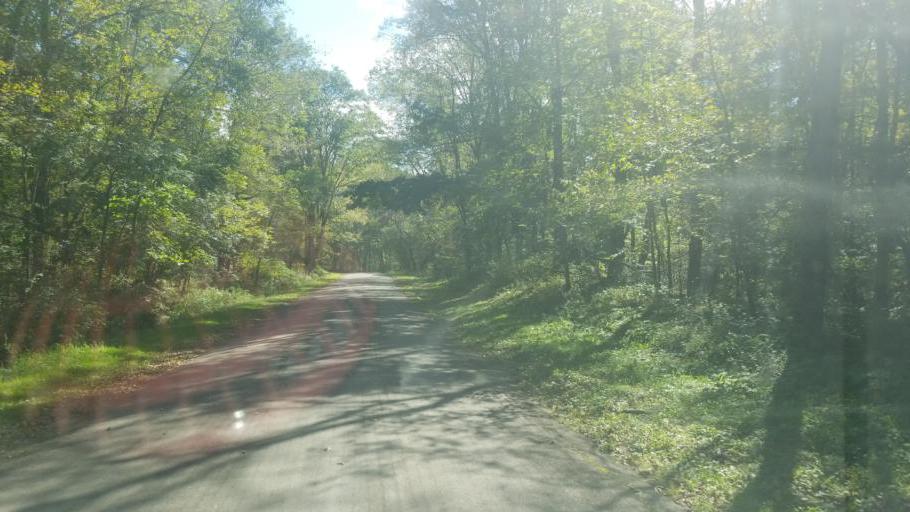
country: US
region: New York
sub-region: Allegany County
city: Cuba
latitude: 42.1692
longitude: -78.3349
